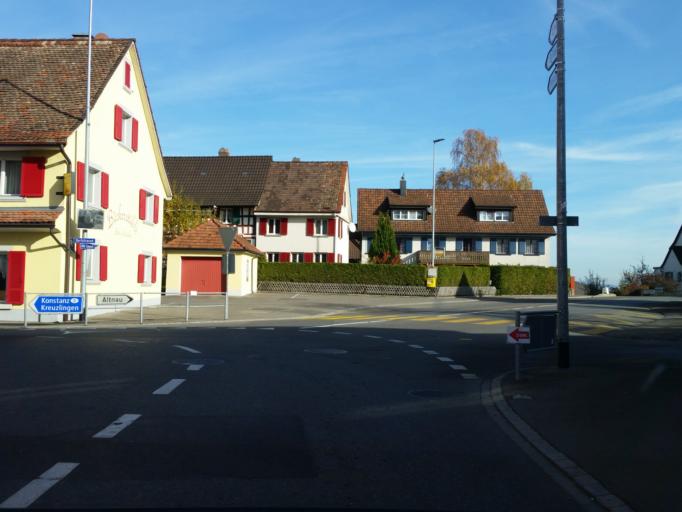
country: CH
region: Thurgau
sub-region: Kreuzlingen District
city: Munsterlingen
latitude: 47.6301
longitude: 9.2263
